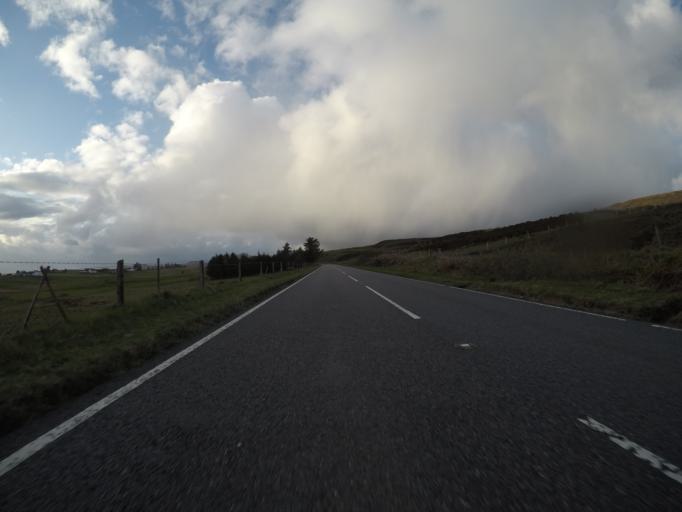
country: GB
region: Scotland
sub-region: Highland
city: Portree
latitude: 57.5577
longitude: -6.3637
